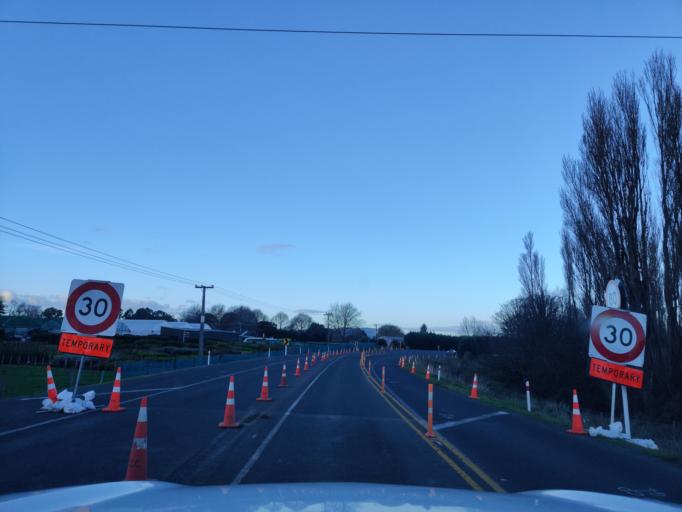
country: NZ
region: Waikato
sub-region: Waipa District
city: Cambridge
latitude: -37.8886
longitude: 175.4367
